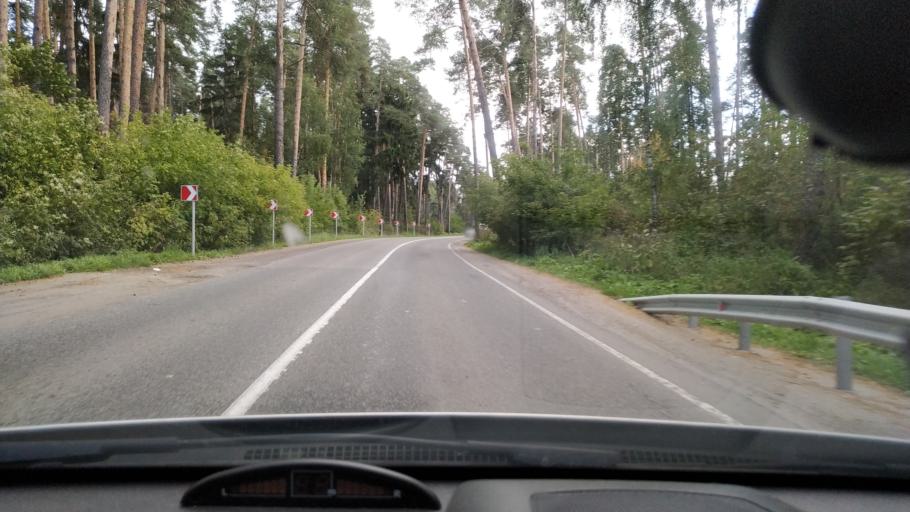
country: RU
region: Moskovskaya
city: Zheleznodorozhnyy
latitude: 55.7988
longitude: 38.0286
